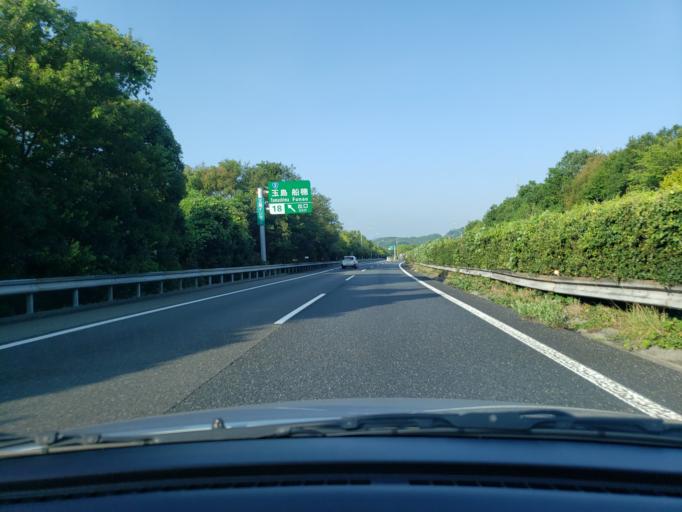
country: JP
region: Okayama
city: Kurashiki
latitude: 34.5870
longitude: 133.6911
